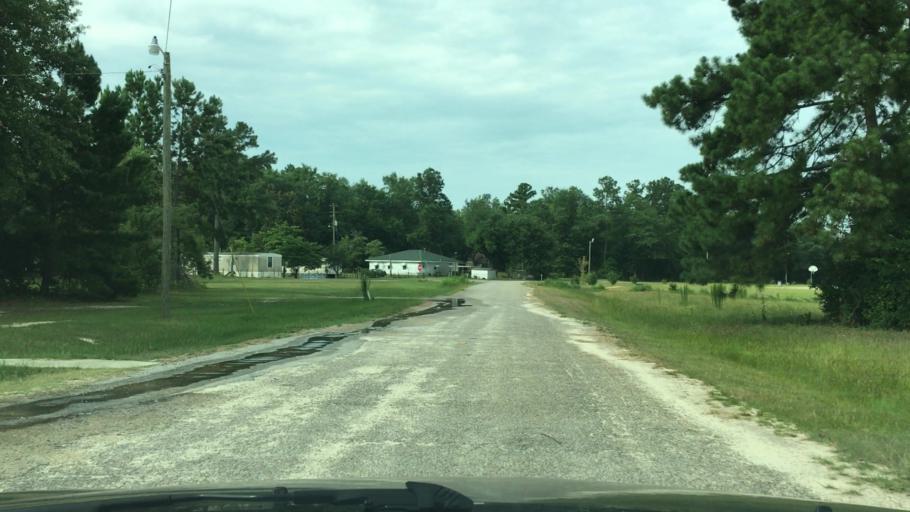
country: US
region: South Carolina
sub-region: Barnwell County
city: Williston
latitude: 33.6591
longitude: -81.3670
